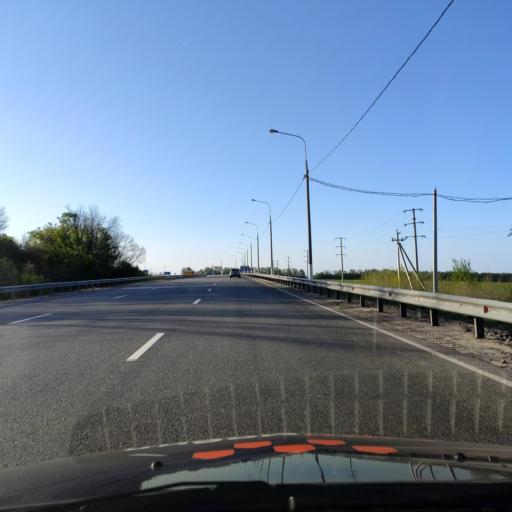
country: RU
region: Lipetsk
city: Yelets
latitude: 52.5471
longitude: 38.7157
